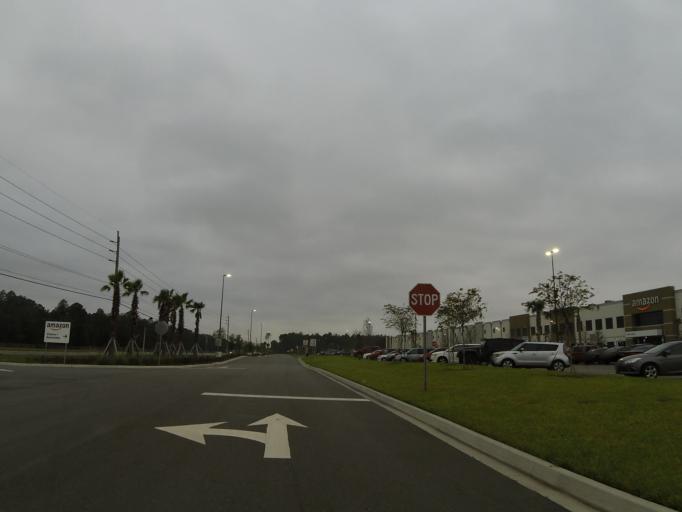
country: US
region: Florida
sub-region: Duval County
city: Baldwin
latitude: 30.2488
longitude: -81.8669
